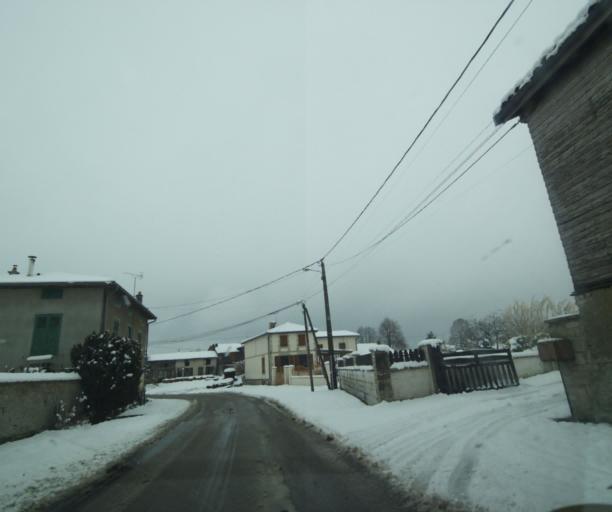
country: FR
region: Champagne-Ardenne
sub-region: Departement de la Haute-Marne
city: Montier-en-Der
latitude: 48.5076
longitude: 4.7842
